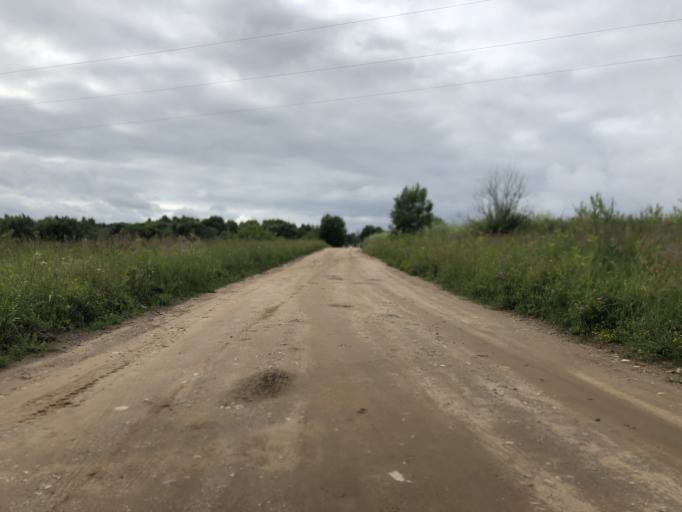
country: RU
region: Tverskaya
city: Rzhev
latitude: 56.2353
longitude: 34.3761
